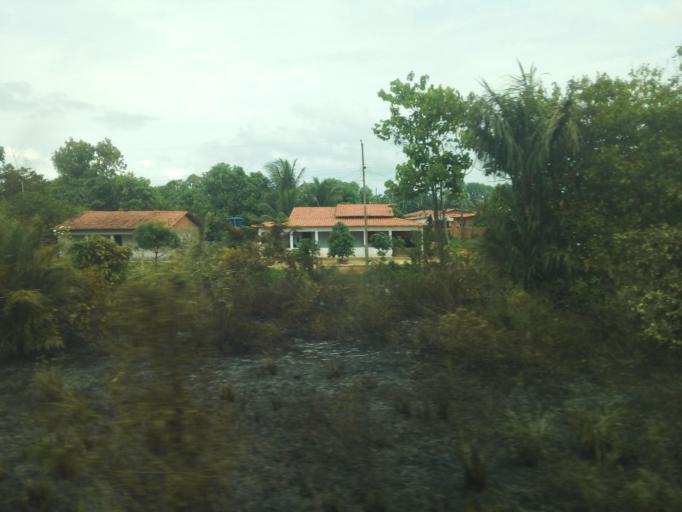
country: BR
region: Maranhao
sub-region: Itapecuru Mirim
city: Itapecuru Mirim
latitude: -3.3192
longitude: -44.4813
